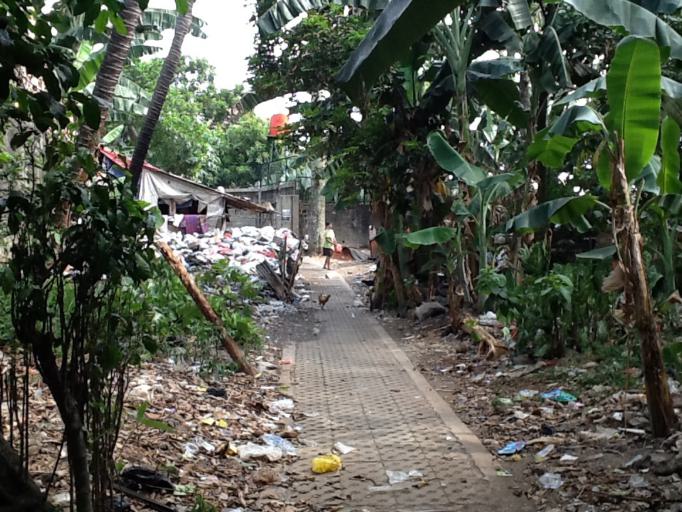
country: ID
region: West Java
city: Pamulang
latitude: -6.3127
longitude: 106.7779
